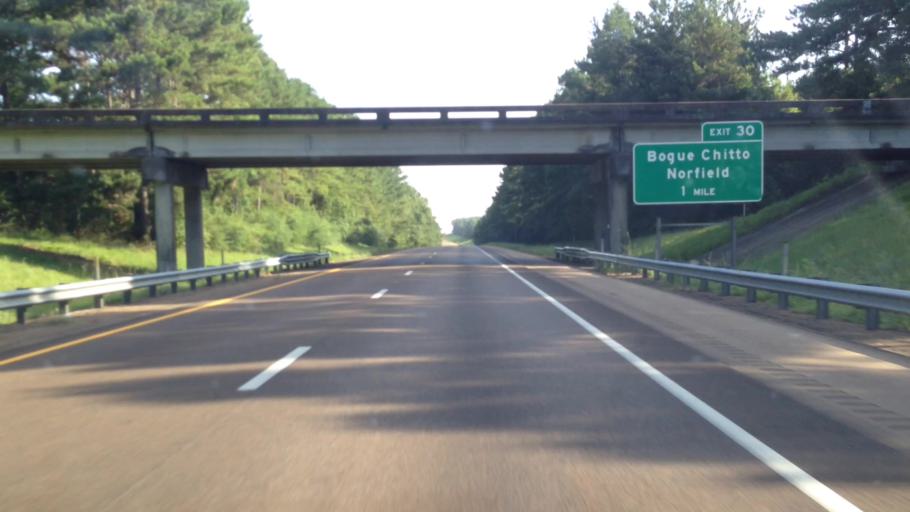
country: US
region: Mississippi
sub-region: Pike County
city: Summit
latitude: 31.4074
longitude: -90.4792
